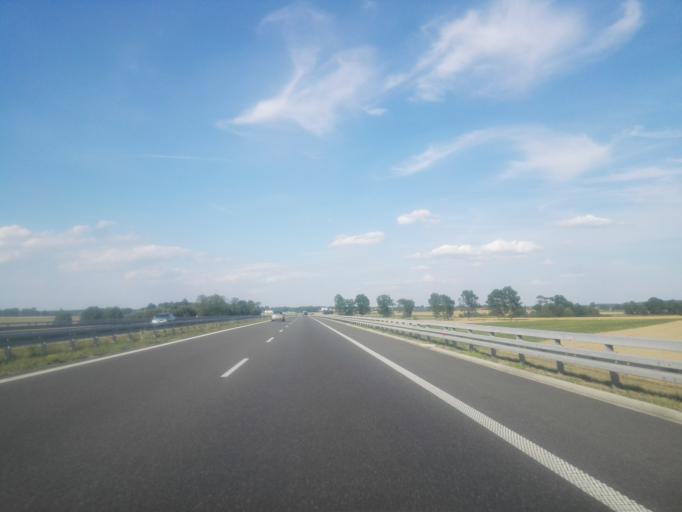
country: PL
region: Lower Silesian Voivodeship
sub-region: Powiat olesnicki
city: Bierutow
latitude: 51.2472
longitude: 17.5169
